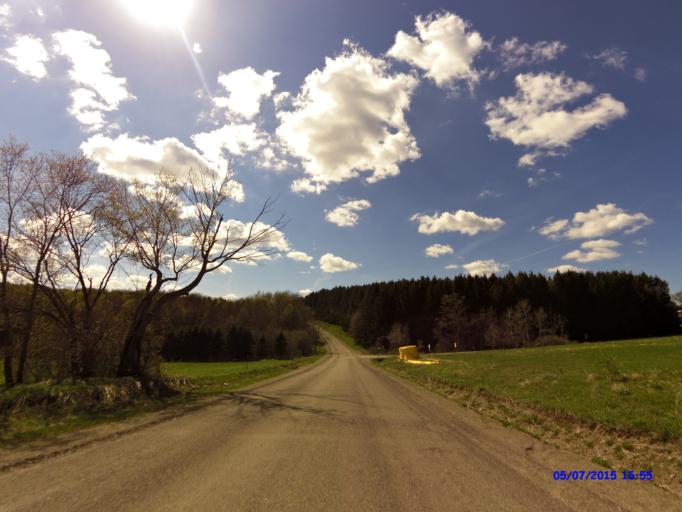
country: US
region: New York
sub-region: Cattaraugus County
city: Franklinville
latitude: 42.3157
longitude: -78.5594
